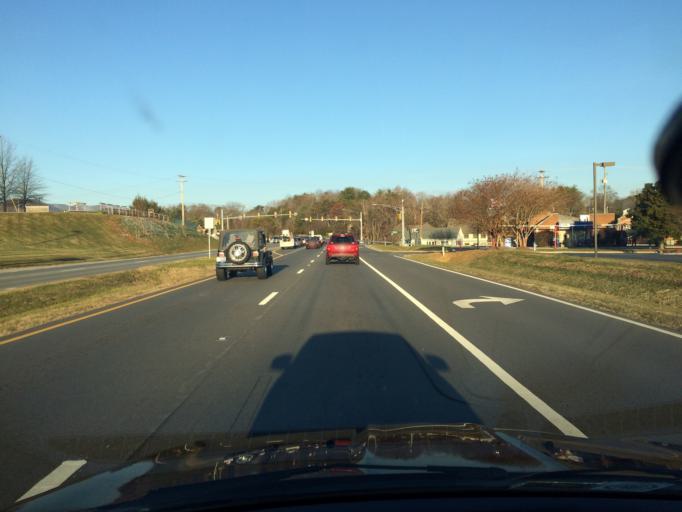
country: US
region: Virginia
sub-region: Roanoke County
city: Cave Spring
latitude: 37.2266
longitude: -79.9985
